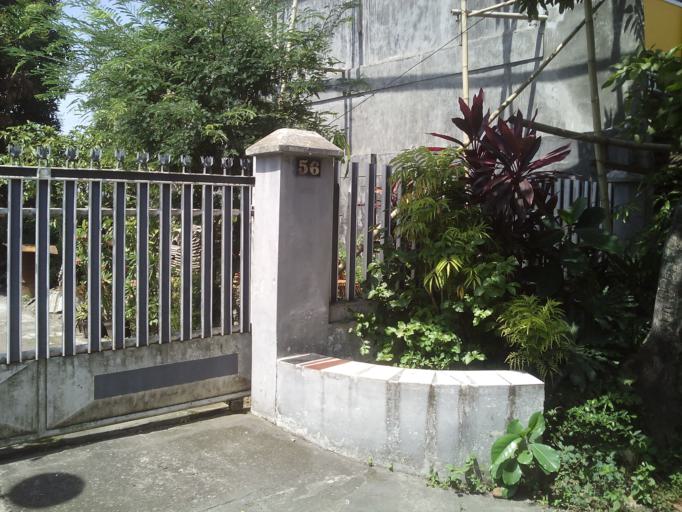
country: ID
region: East Java
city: Sumbersari Wetan
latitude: -8.1774
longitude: 113.7217
